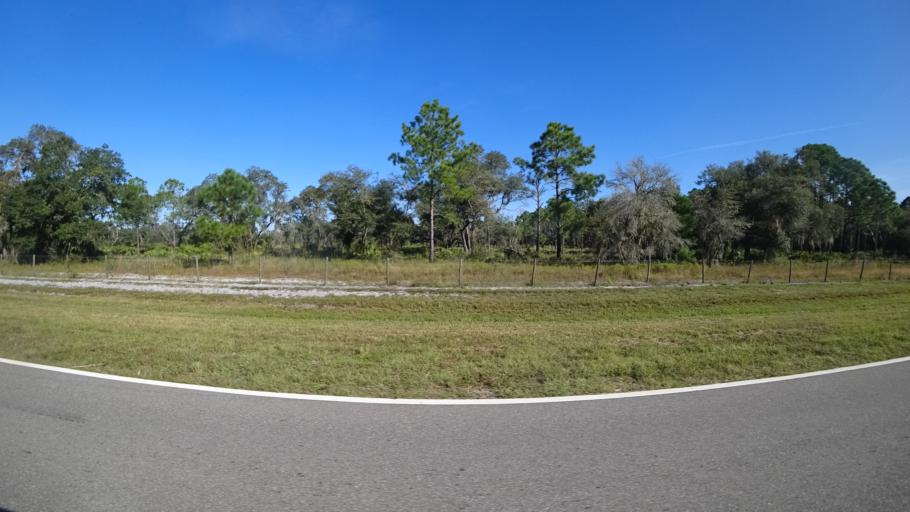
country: US
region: Florida
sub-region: Hillsborough County
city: Sun City Center
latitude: 27.6575
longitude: -82.3724
